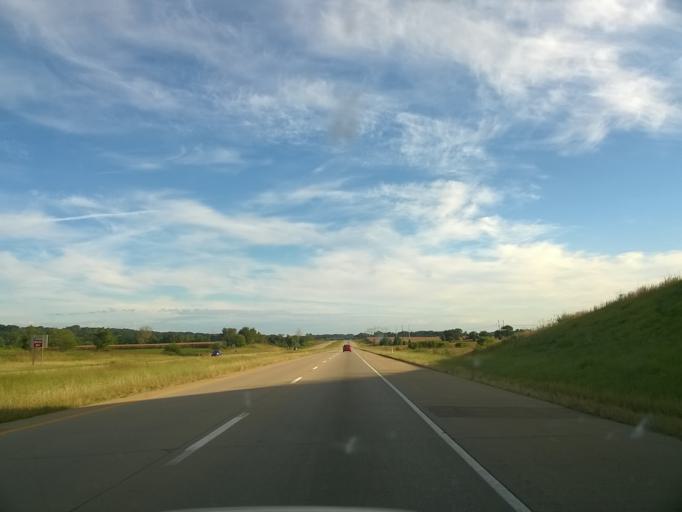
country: US
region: Indiana
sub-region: Vanderburgh County
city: Darmstadt
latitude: 38.1395
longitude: -87.4727
